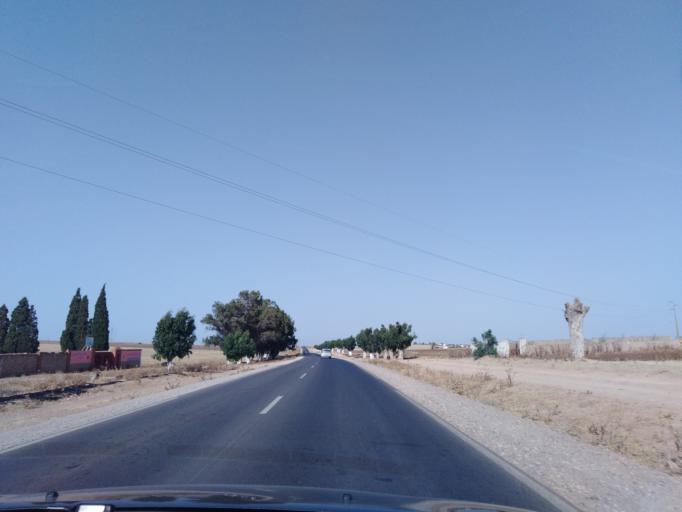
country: MA
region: Doukkala-Abda
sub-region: Safi
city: Safi
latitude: 32.2599
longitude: -8.9660
